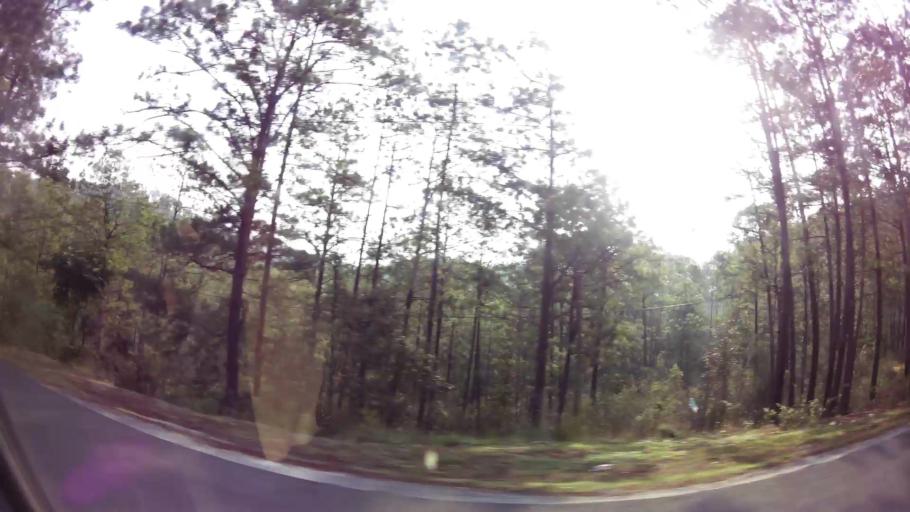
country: HN
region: Francisco Morazan
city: Zambrano
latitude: 14.2852
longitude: -87.4569
